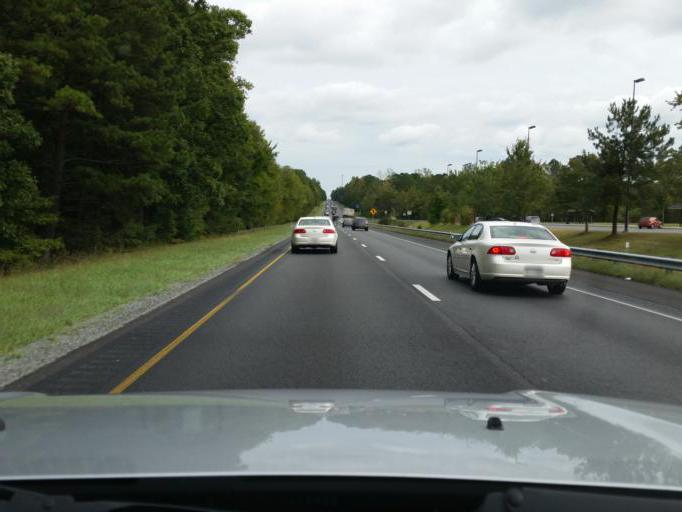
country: US
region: Virginia
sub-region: New Kent County
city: New Kent
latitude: 37.4976
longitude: -77.0432
